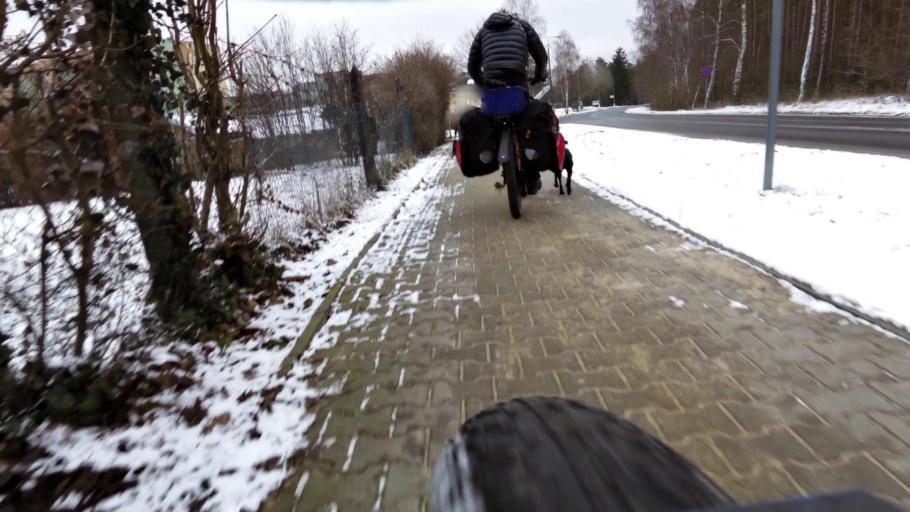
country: PL
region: West Pomeranian Voivodeship
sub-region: Powiat walecki
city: Miroslawiec
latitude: 53.3700
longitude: 16.0849
